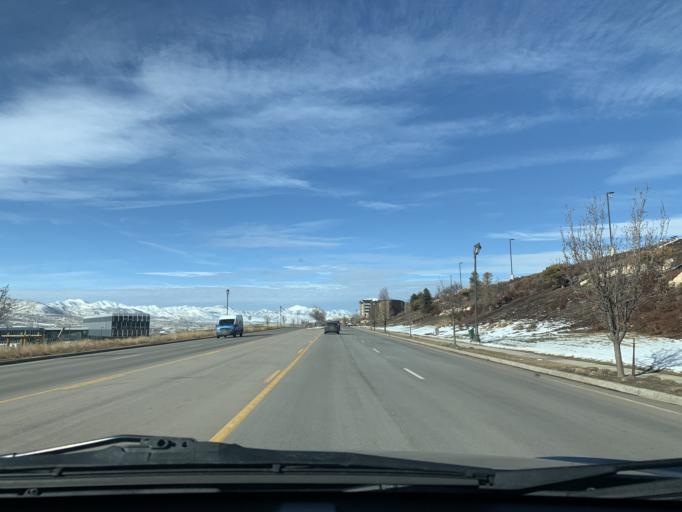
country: US
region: Utah
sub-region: Utah County
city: Lehi
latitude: 40.4336
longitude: -111.8864
